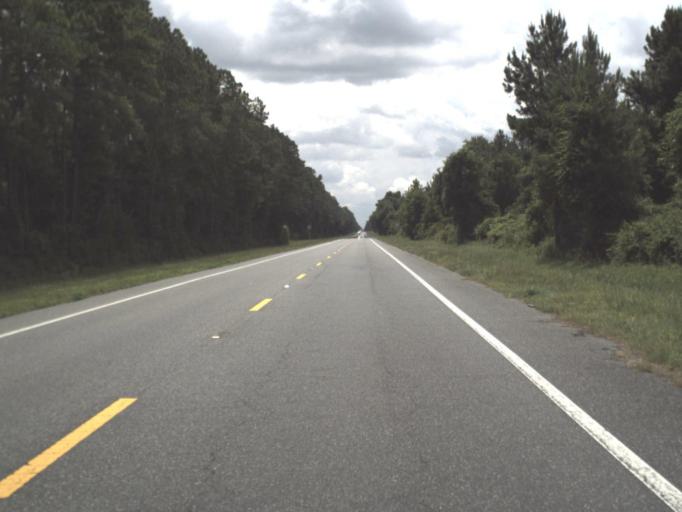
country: US
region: Florida
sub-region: Columbia County
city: Watertown
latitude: 30.1383
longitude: -82.5349
